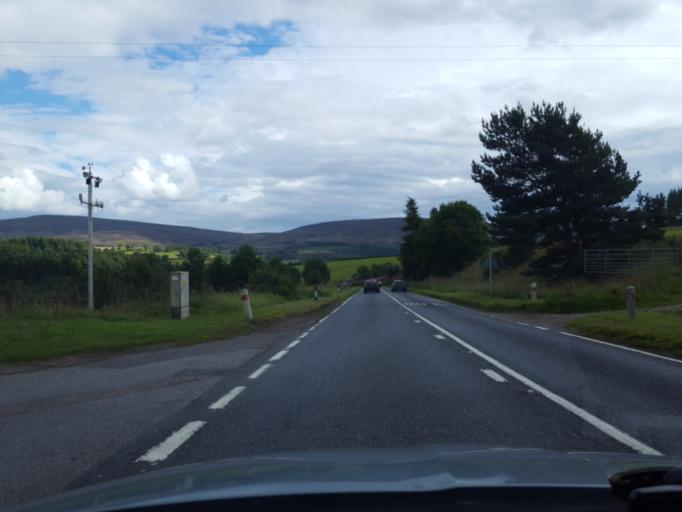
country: GB
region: Scotland
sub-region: Moray
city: Rothes
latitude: 57.4088
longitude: -3.3789
